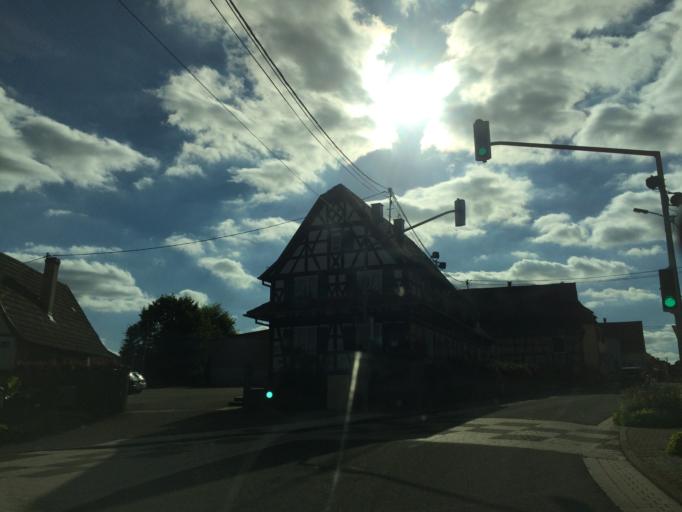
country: FR
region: Alsace
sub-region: Departement du Bas-Rhin
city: Soufflenheim
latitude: 48.8296
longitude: 7.9623
